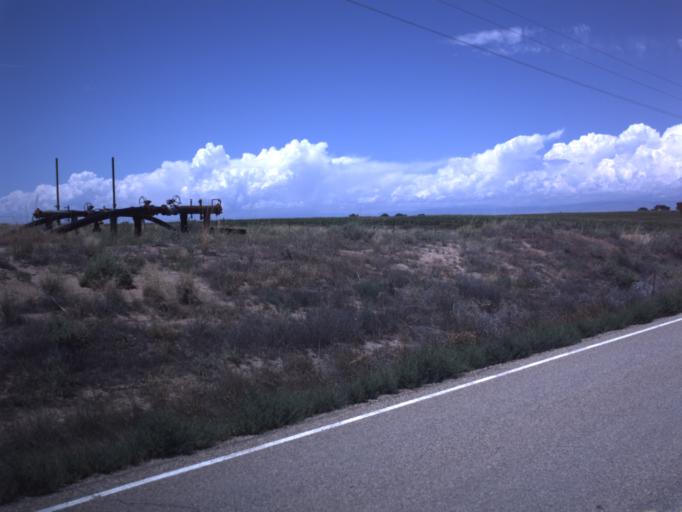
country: US
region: Utah
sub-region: Uintah County
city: Naples
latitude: 40.1358
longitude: -109.6639
